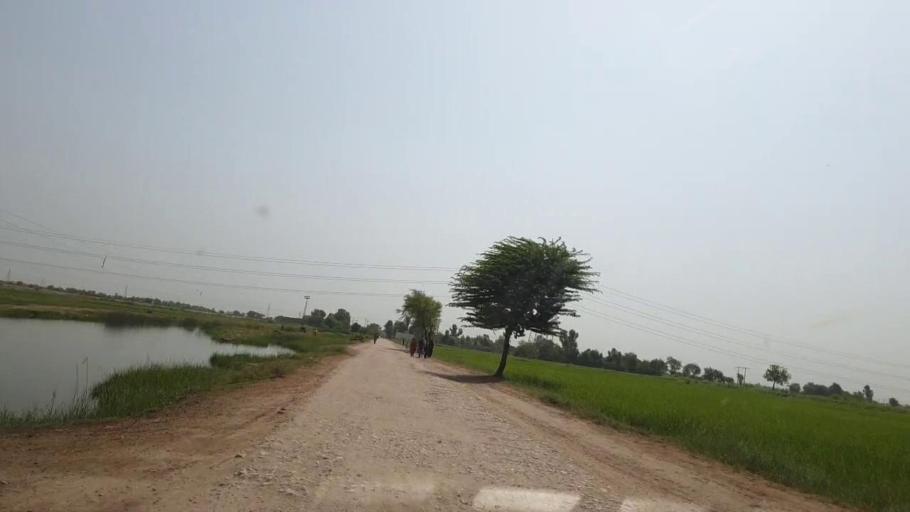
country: PK
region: Sindh
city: Lakhi
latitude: 27.8800
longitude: 68.6762
